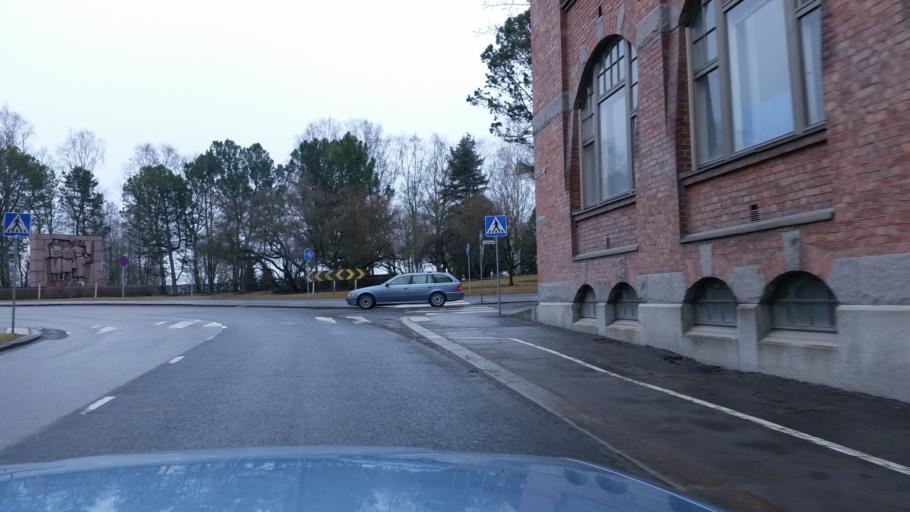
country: FI
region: Pirkanmaa
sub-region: Tampere
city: Tampere
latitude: 61.4915
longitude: 23.7537
